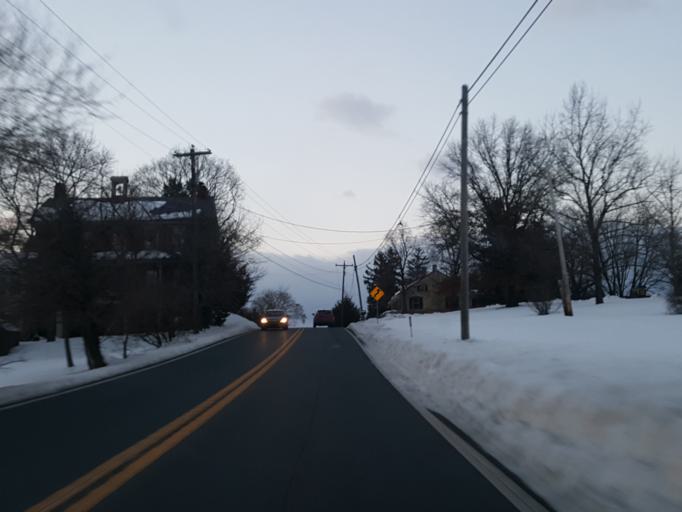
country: US
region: Pennsylvania
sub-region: Dauphin County
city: Palmdale
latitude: 40.3579
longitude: -76.6407
